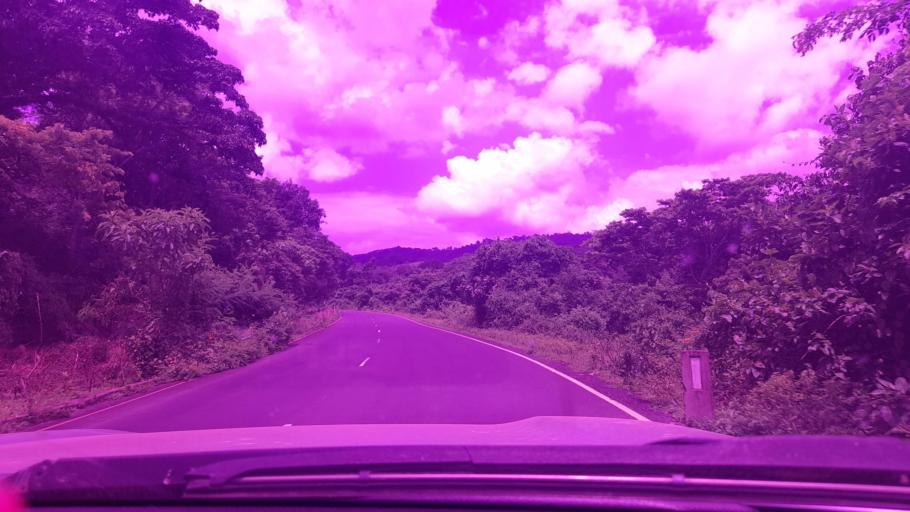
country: ET
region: Oromiya
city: Metu
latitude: 8.3325
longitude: 35.7681
